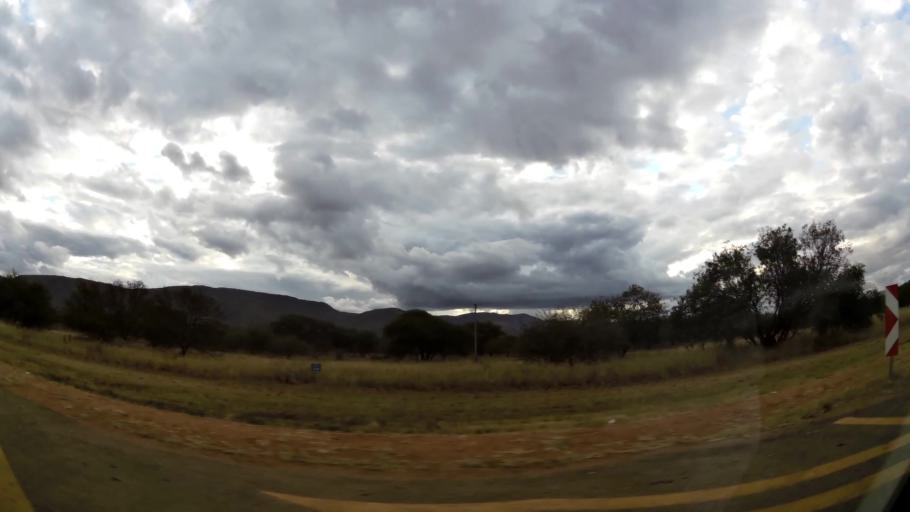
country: ZA
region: Limpopo
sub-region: Waterberg District Municipality
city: Mokopane
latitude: -24.2282
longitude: 29.0005
